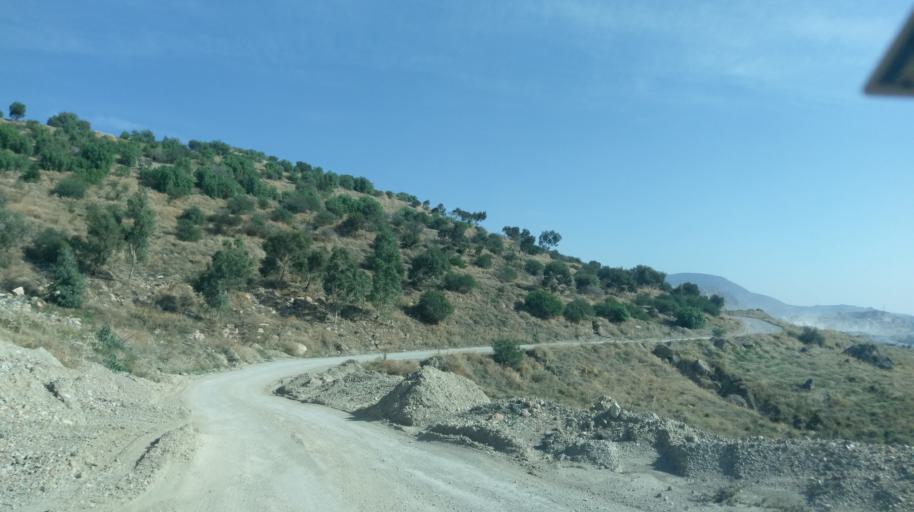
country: CY
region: Lefkosia
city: Nicosia
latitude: 35.2672
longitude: 33.4339
